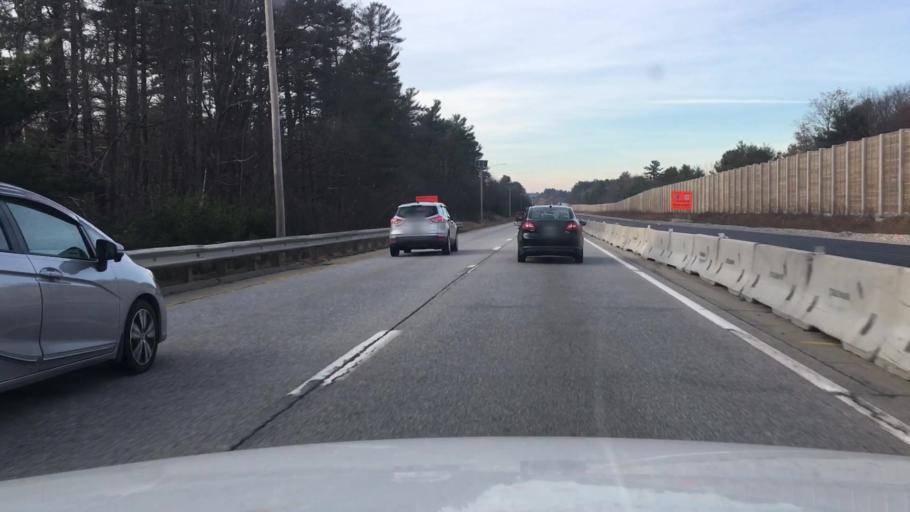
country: US
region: New Hampshire
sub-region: Rockingham County
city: Auburn
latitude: 42.9445
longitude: -71.3898
